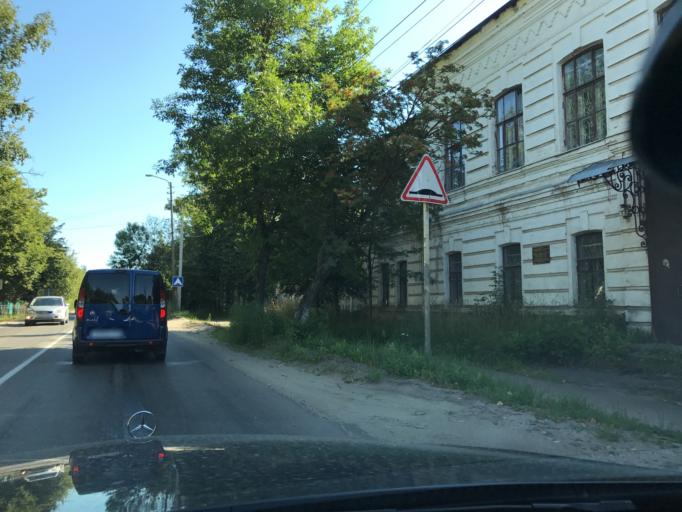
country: RU
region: Vladimir
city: Kirzhach
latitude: 56.1643
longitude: 38.8823
